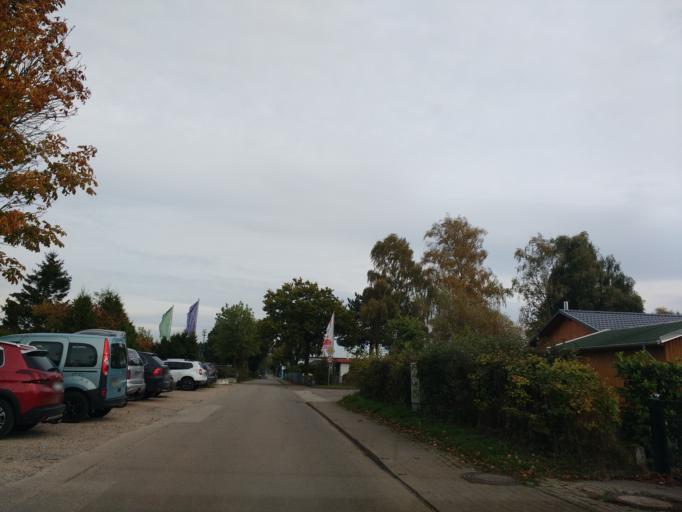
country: DE
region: Schleswig-Holstein
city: Gromitz
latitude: 54.1620
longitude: 10.9963
